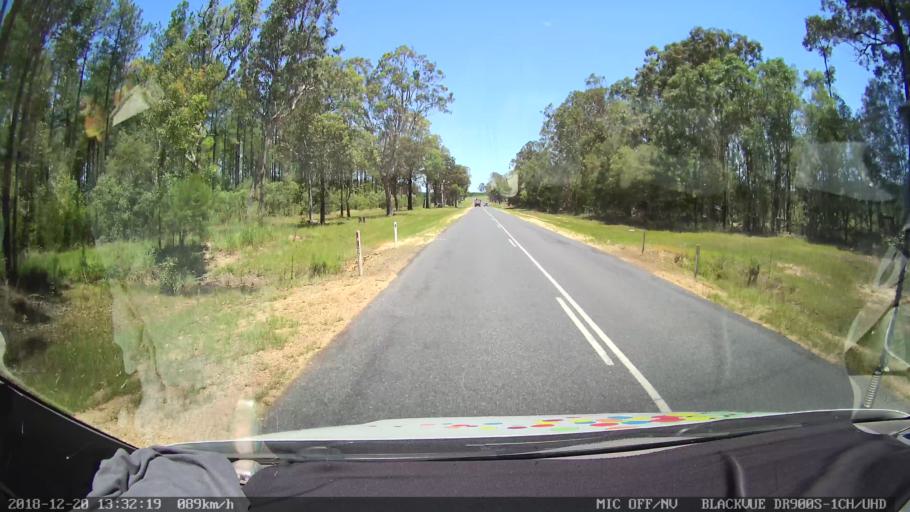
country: AU
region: New South Wales
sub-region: Clarence Valley
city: Gordon
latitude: -29.2302
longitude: 152.9890
